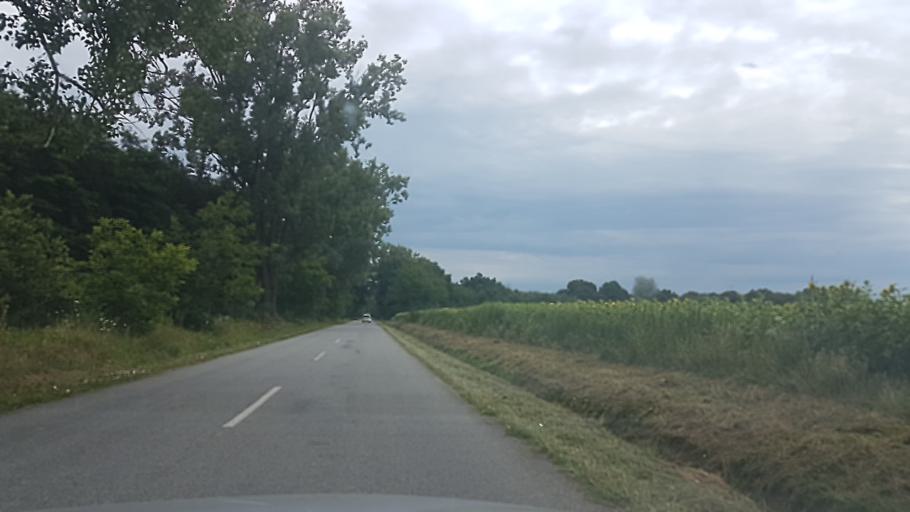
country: HU
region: Somogy
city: Barcs
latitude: 45.9501
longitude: 17.6250
